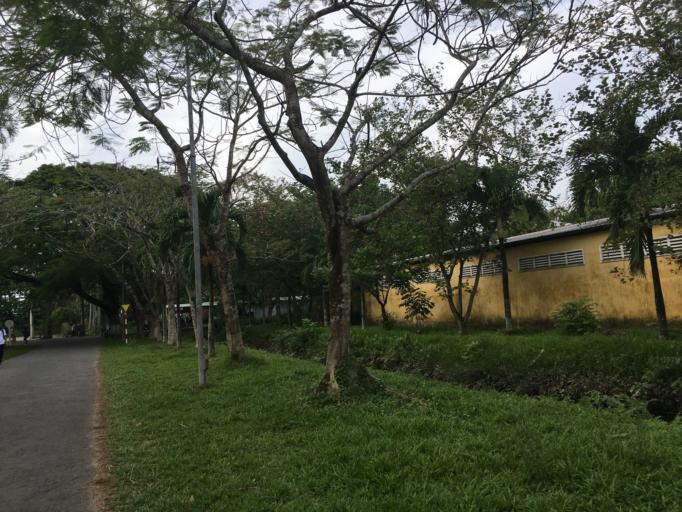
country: VN
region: Can Tho
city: Can Tho
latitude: 10.0320
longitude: 105.7695
